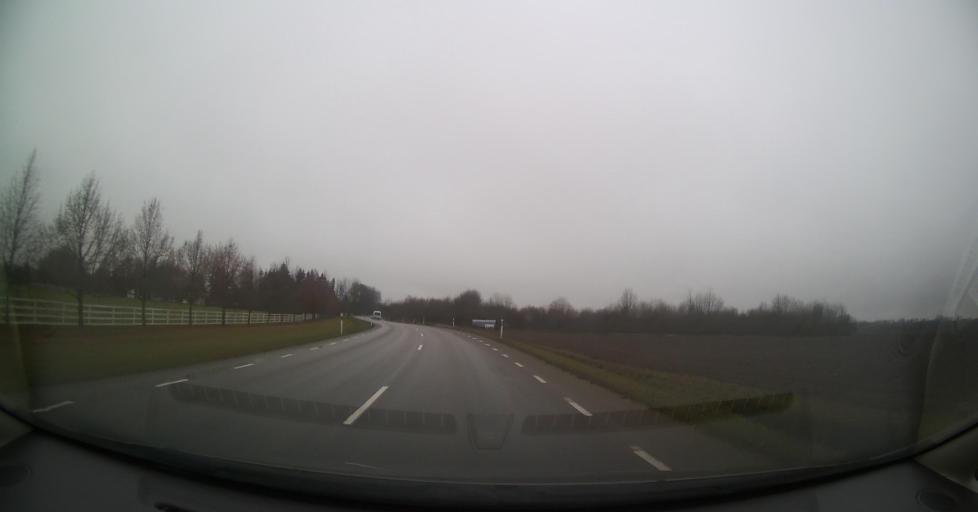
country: EE
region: Tartu
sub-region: Tartu linn
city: Tartu
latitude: 58.3877
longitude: 26.7928
